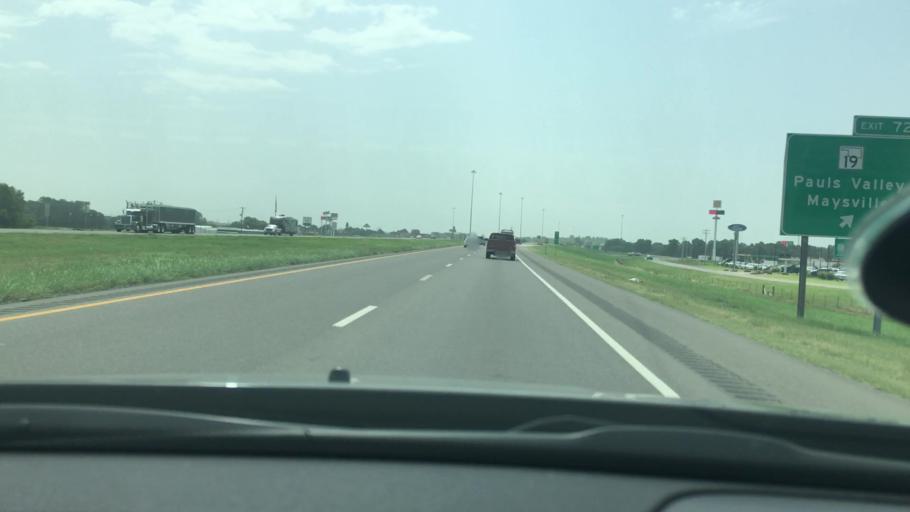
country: US
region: Oklahoma
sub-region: Garvin County
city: Pauls Valley
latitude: 34.7453
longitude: -97.2690
